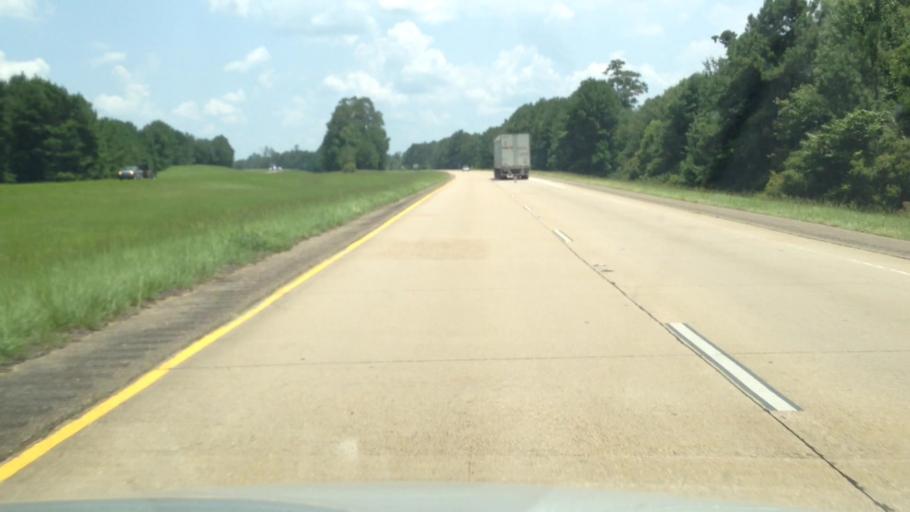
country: US
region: Louisiana
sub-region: Rapides Parish
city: Lecompte
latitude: 31.0391
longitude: -92.4154
